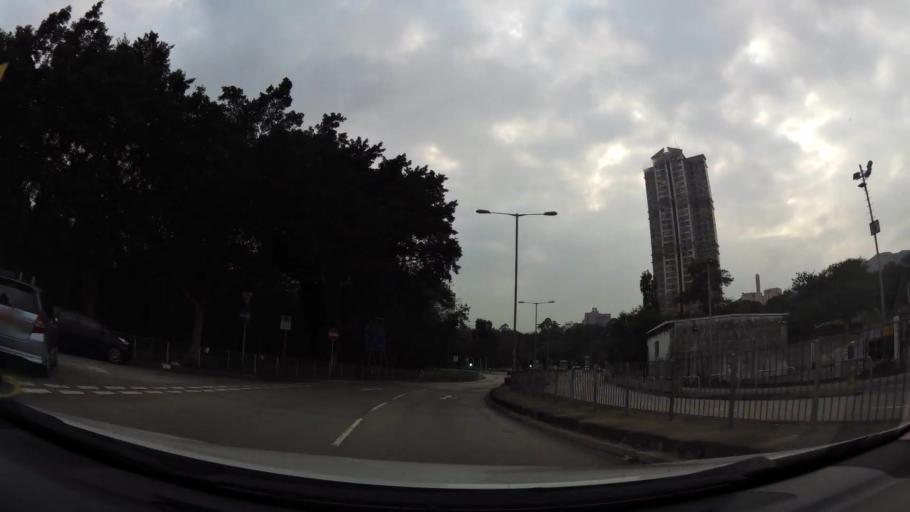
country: HK
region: Tai Po
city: Tai Po
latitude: 22.4567
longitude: 114.1784
